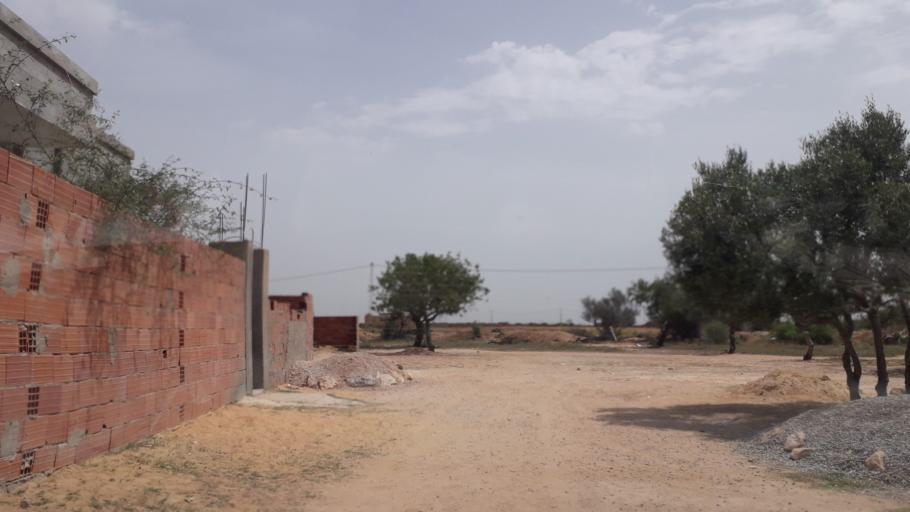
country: TN
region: Safaqis
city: Al Qarmadah
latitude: 34.8447
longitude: 10.7794
